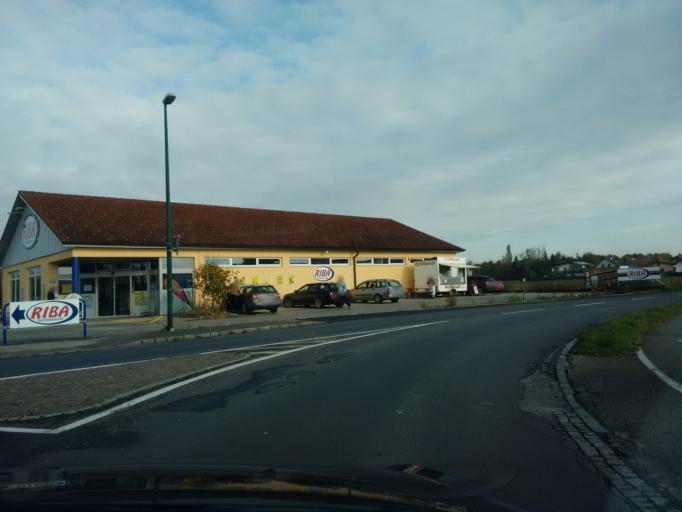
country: AT
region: Upper Austria
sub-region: Wels Stadt
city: Wels
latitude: 48.1797
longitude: 14.0095
